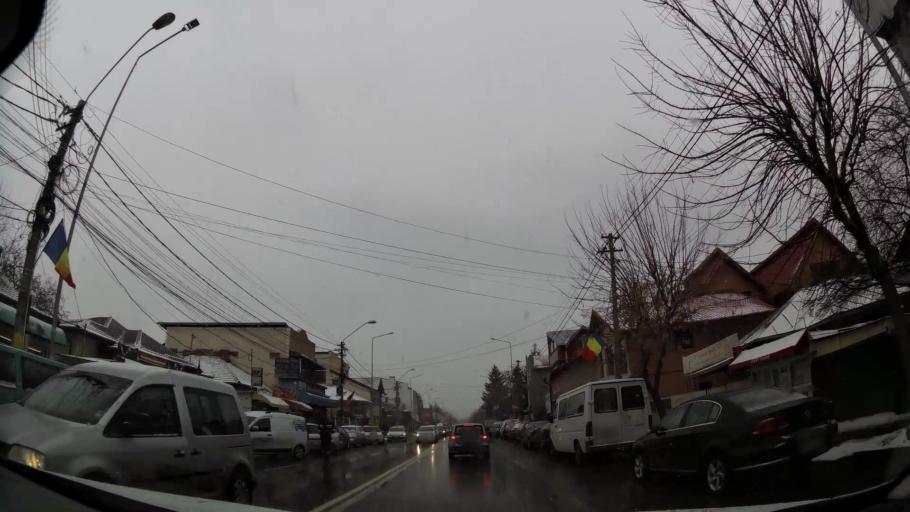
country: RO
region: Dambovita
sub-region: Municipiul Targoviste
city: Targoviste
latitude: 44.9217
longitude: 25.4541
